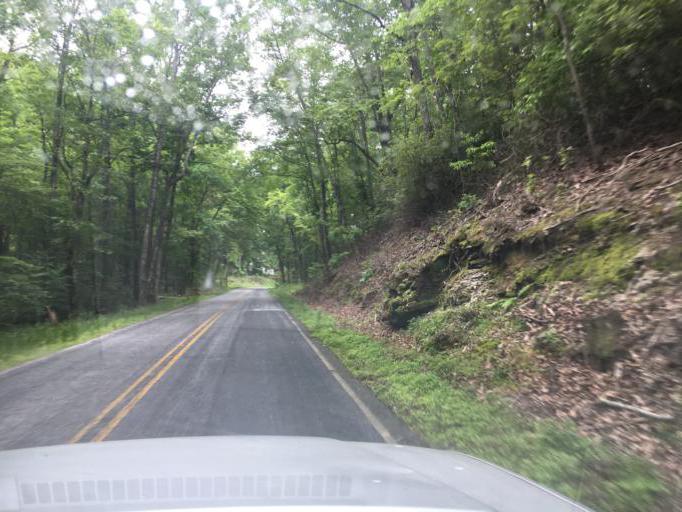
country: US
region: South Carolina
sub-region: Greenville County
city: Tigerville
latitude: 35.1244
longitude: -82.3800
